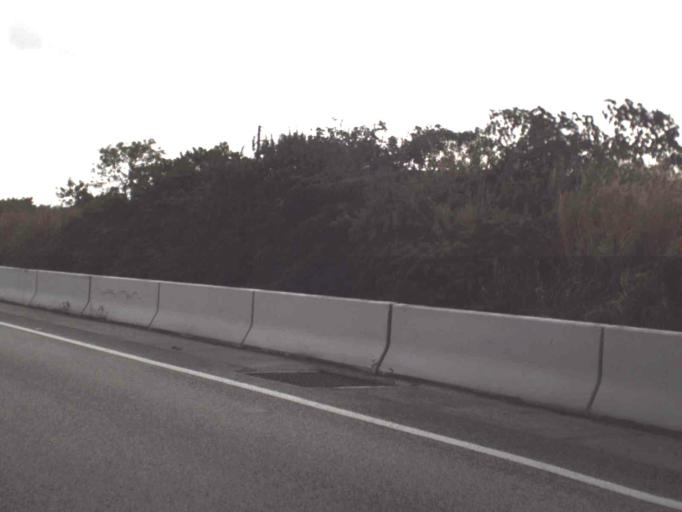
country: US
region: Florida
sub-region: Miami-Dade County
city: Lake Lucerne
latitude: 25.9658
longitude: -80.2296
